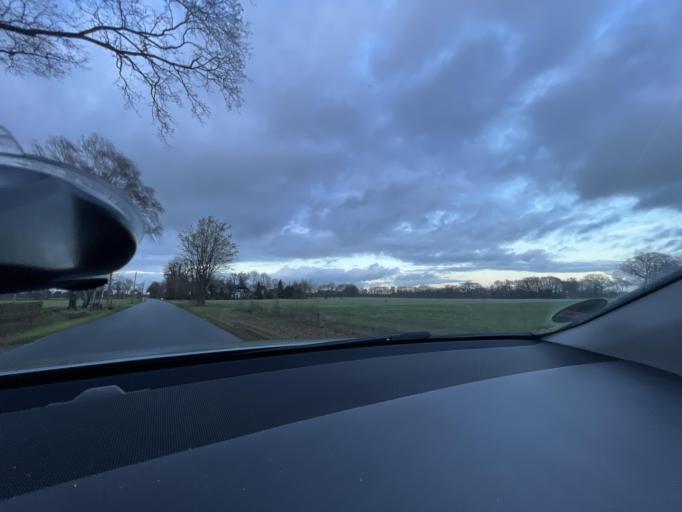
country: DE
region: Lower Saxony
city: Hatten
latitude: 53.0561
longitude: 8.3391
